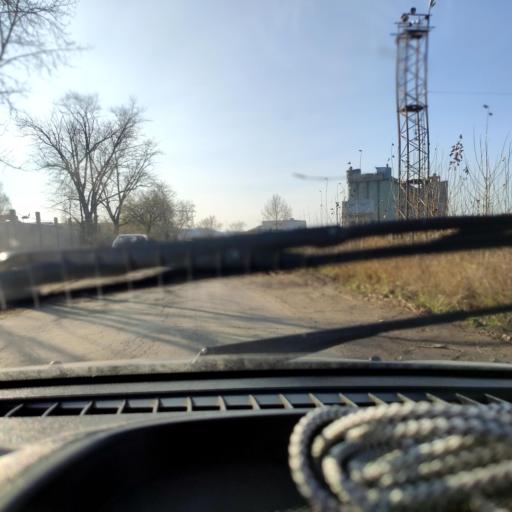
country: RU
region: Samara
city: Zhigulevsk
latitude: 53.4733
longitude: 49.5011
